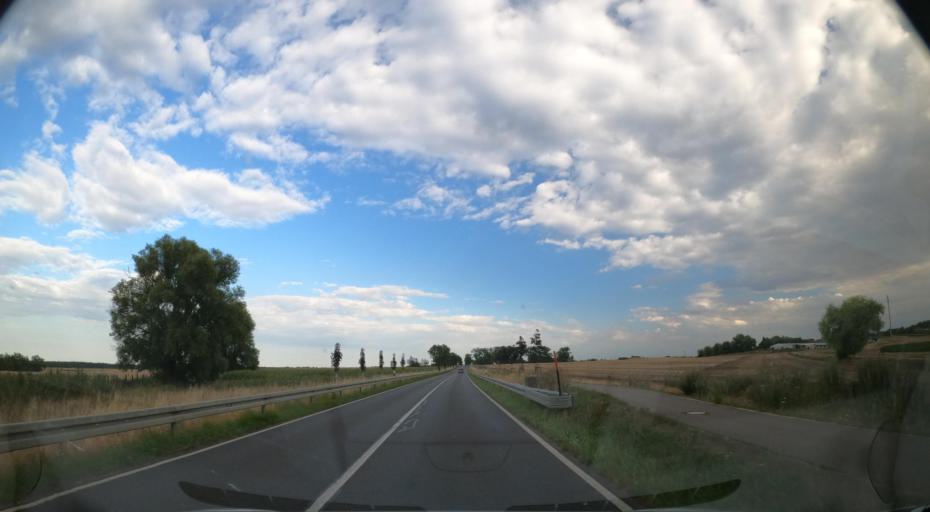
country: DE
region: Mecklenburg-Vorpommern
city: Viereck
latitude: 53.4913
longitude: 14.0927
